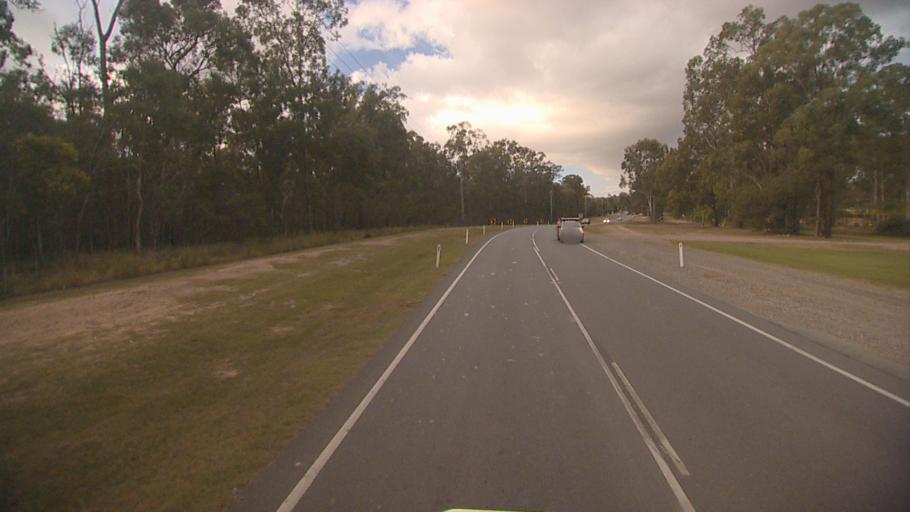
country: AU
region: Queensland
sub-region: Logan
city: Park Ridge South
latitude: -27.7091
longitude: 152.9993
